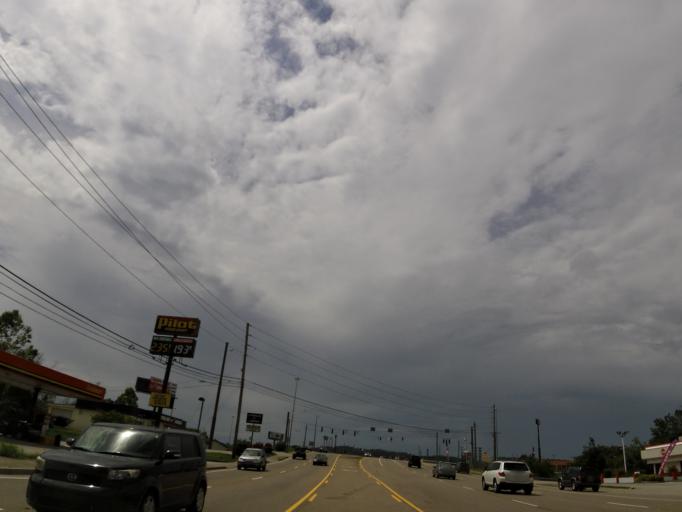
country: US
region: Tennessee
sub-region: Knox County
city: Farragut
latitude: 35.9047
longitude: -84.1432
